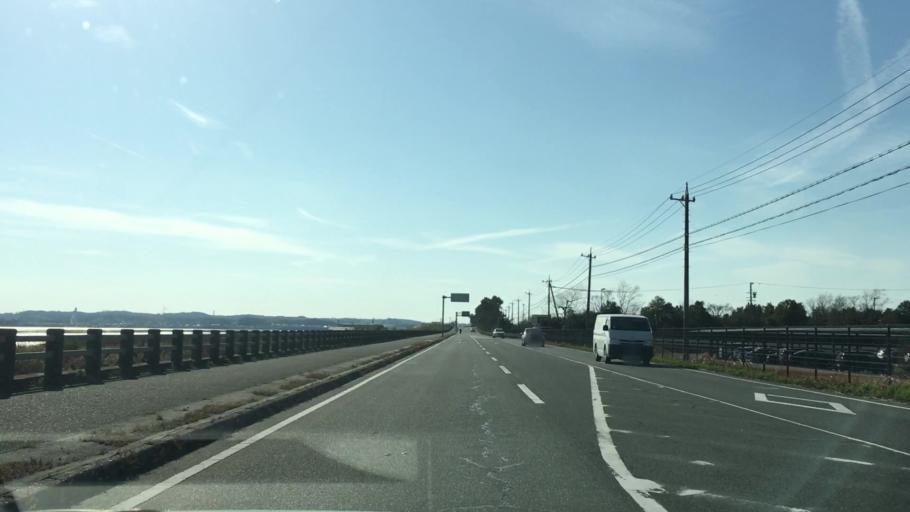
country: JP
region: Shizuoka
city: Kosai-shi
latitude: 34.7121
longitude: 137.5954
